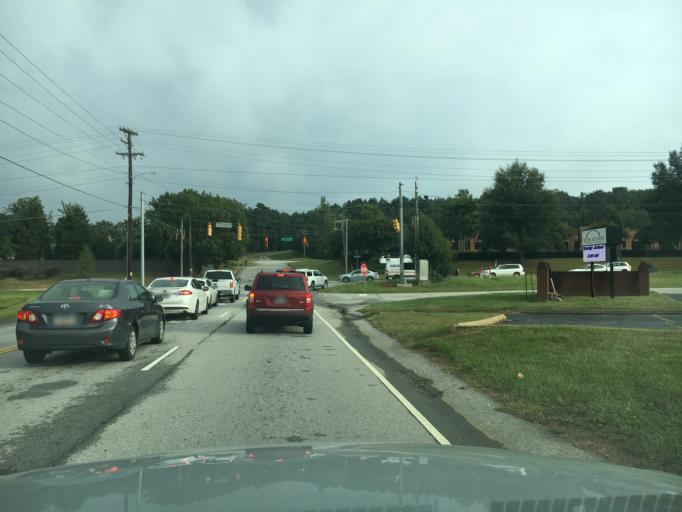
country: US
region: South Carolina
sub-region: Greenville County
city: Wade Hampton
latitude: 34.8453
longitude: -82.3101
